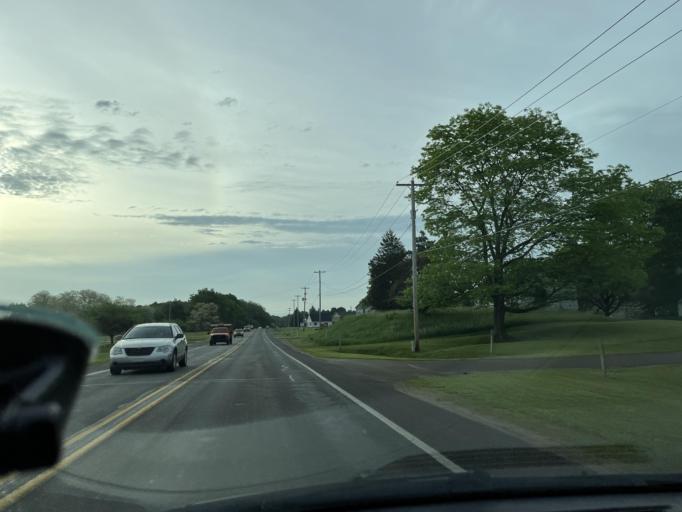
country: US
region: Michigan
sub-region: Barry County
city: Hastings
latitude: 42.6439
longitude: -85.3126
